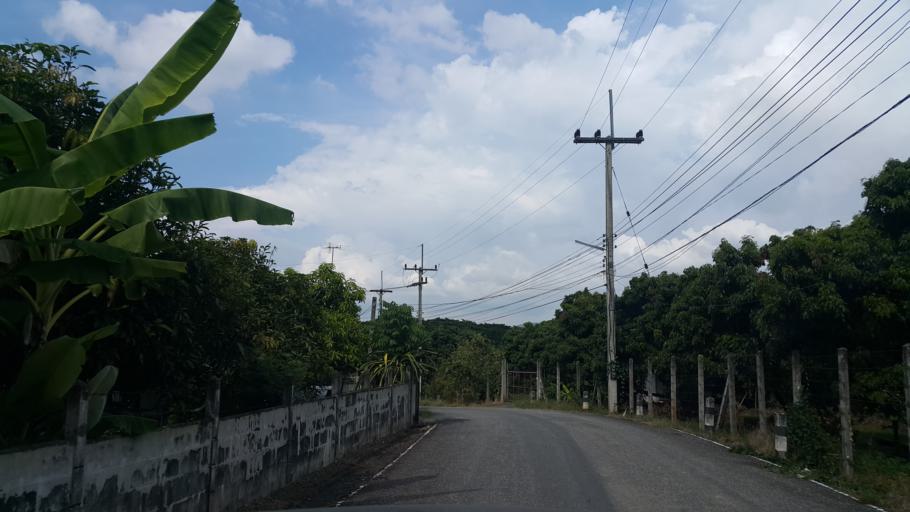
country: TH
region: Chiang Mai
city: San Sai
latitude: 18.8931
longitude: 99.1209
